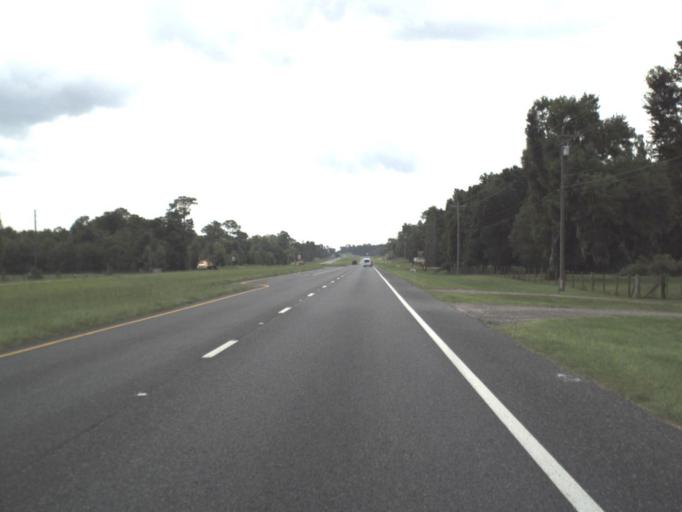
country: US
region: Florida
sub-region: Levy County
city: Bronson
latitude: 29.4360
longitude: -82.6162
